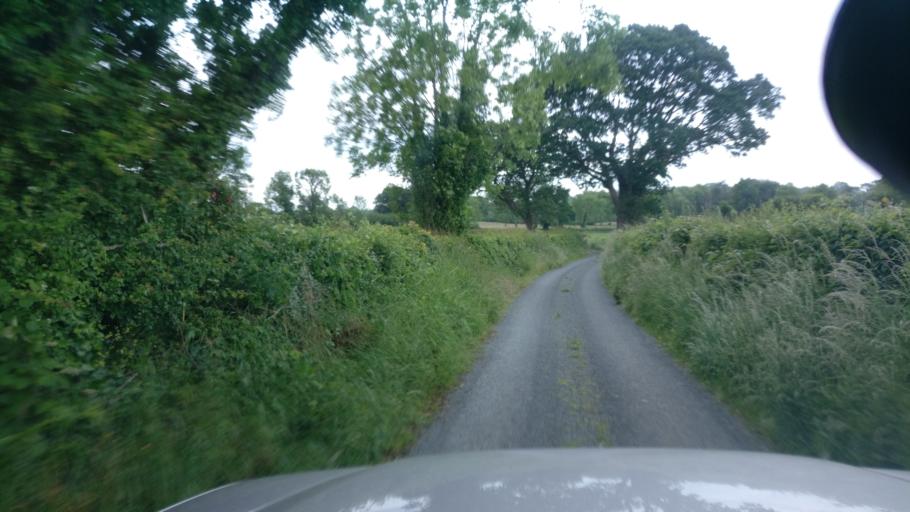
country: IE
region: Connaught
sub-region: County Galway
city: Ballinasloe
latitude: 53.3080
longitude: -8.2574
